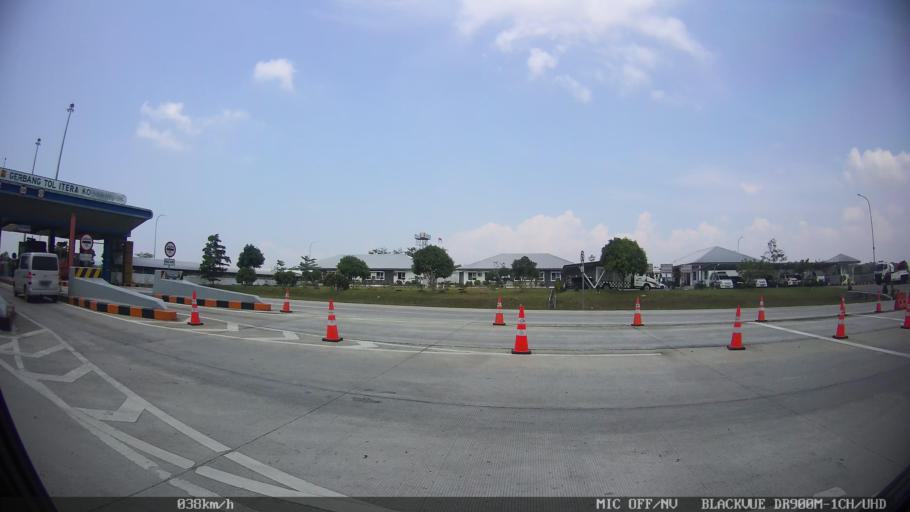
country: ID
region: Lampung
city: Kedaton
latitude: -5.3577
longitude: 105.3273
